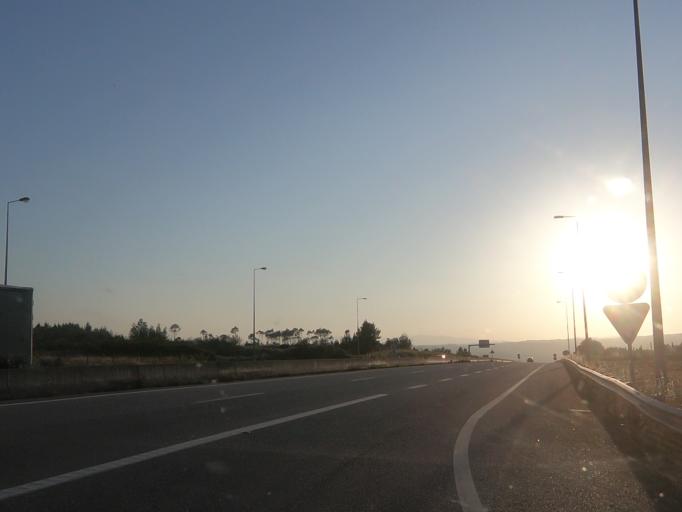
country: PT
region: Viseu
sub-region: Mangualde
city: Mangualde
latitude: 40.6259
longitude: -7.7817
